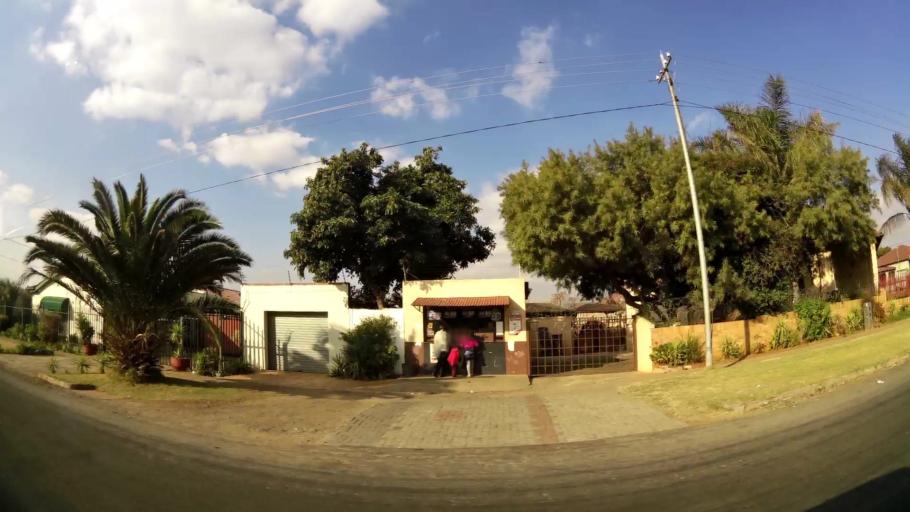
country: ZA
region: Gauteng
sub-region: West Rand District Municipality
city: Krugersdorp
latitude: -26.0921
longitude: 27.7455
